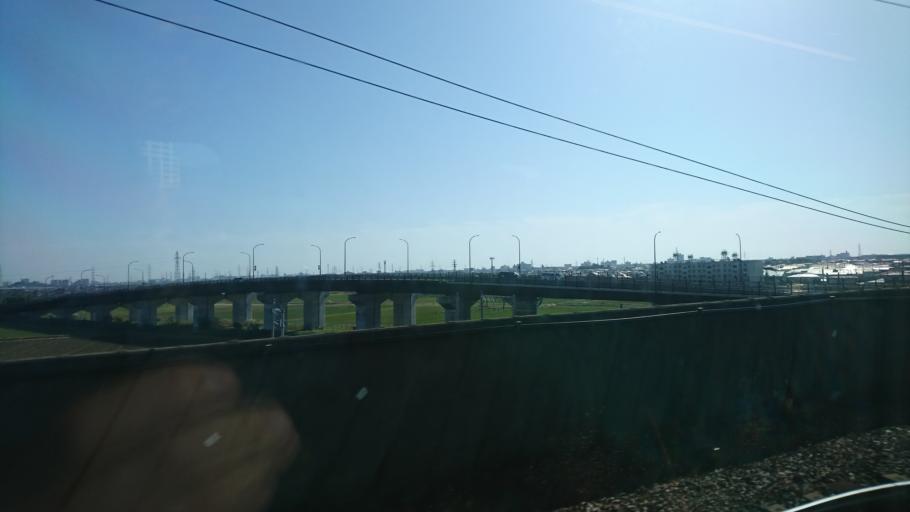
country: JP
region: Miyagi
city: Rifu
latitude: 38.3038
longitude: 140.9589
